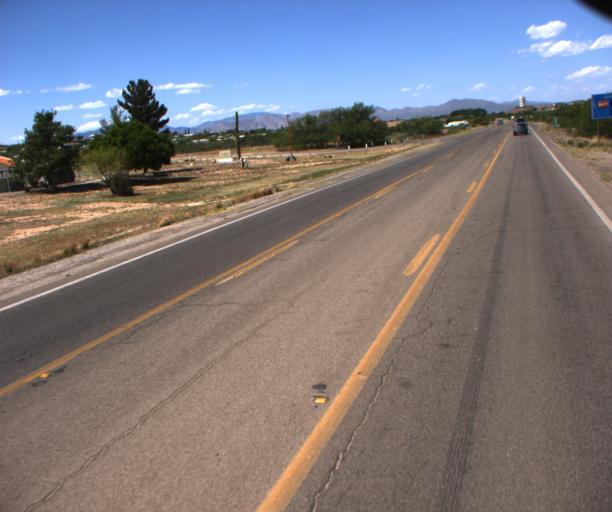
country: US
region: Arizona
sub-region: Cochise County
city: Benson
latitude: 31.9573
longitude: -110.2868
